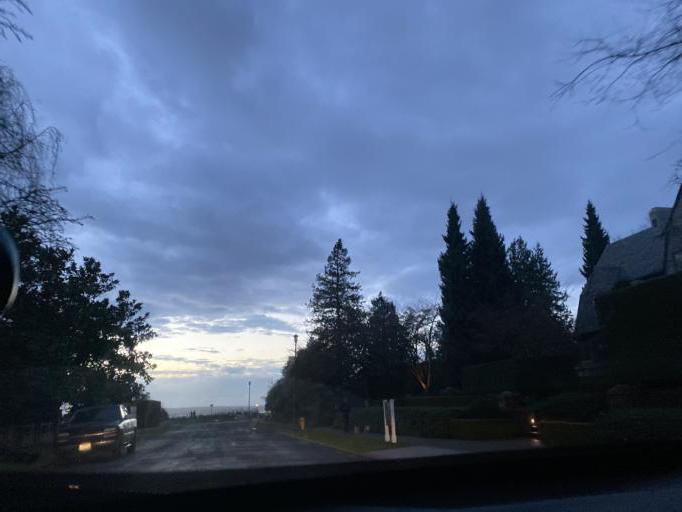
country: US
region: Washington
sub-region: King County
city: Seattle
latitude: 47.6296
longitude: -122.3651
